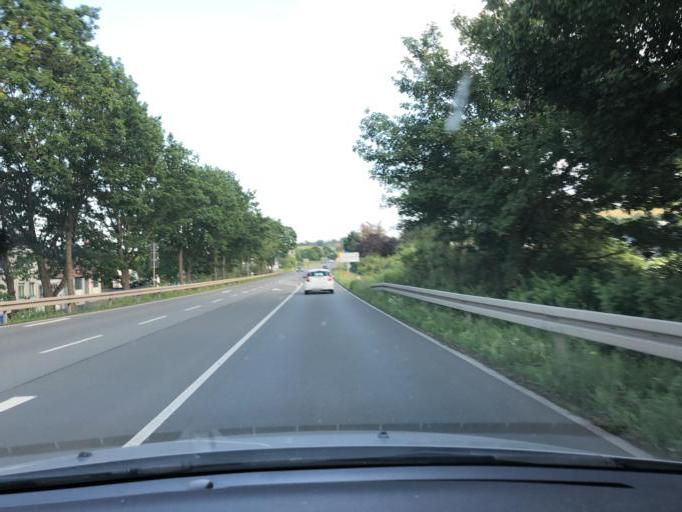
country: DE
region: Hesse
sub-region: Regierungsbezirk Kassel
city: Guxhagen
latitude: 51.2038
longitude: 9.4701
